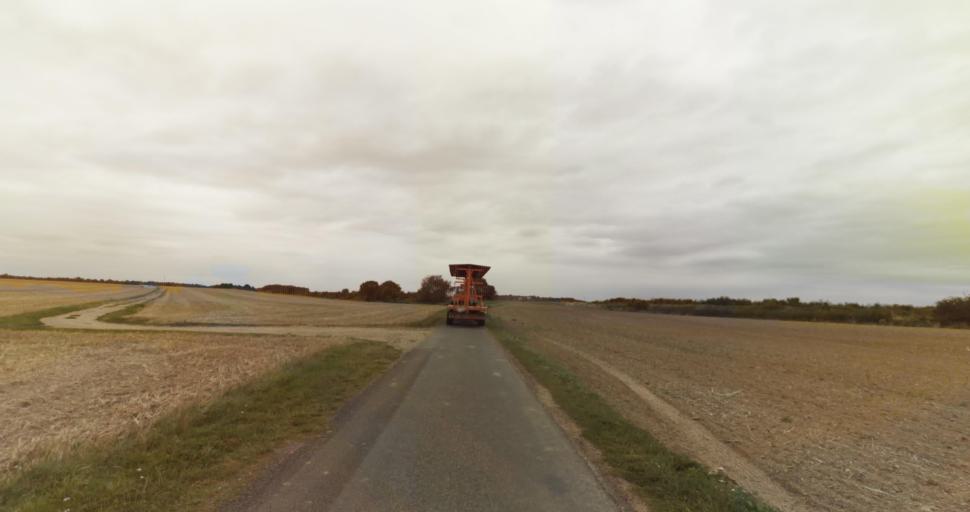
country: FR
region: Haute-Normandie
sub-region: Departement de l'Eure
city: Evreux
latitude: 48.9707
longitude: 1.2212
